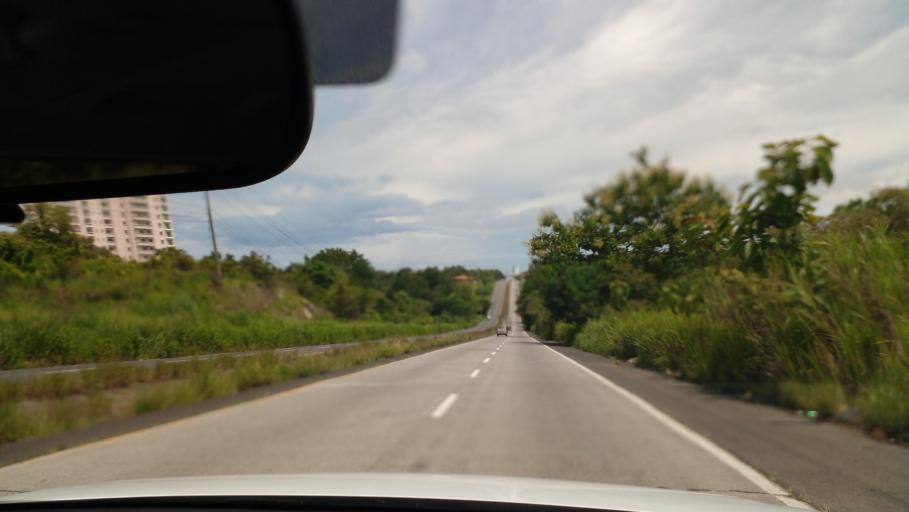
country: PA
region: Panama
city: Nueva Gorgona
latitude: 8.4961
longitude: -79.9582
